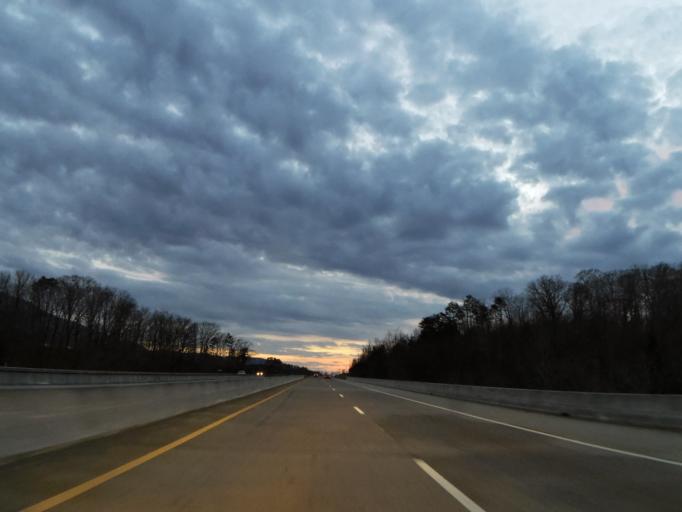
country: US
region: Tennessee
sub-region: McMinn County
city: Etowah
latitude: 35.2408
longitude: -84.5634
